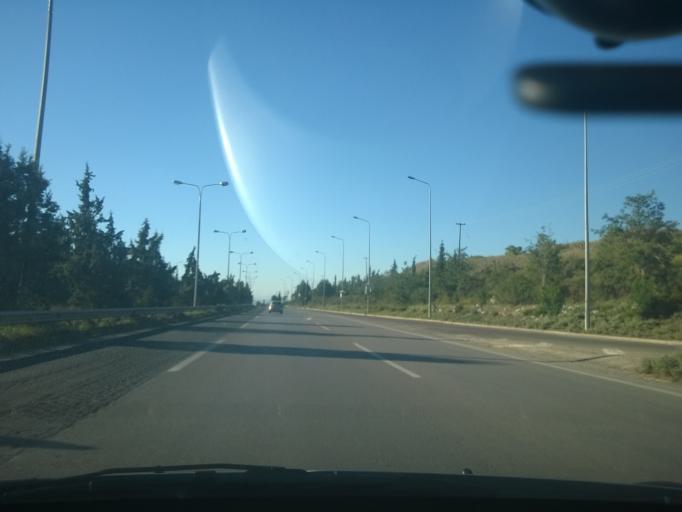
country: GR
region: Central Macedonia
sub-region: Nomos Thessalonikis
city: Pylaia
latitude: 40.5832
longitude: 22.9757
